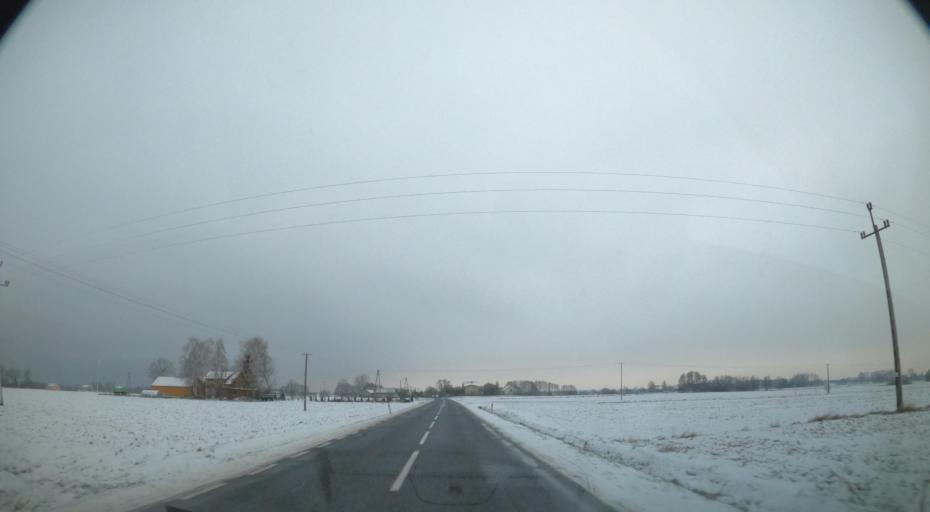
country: PL
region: Masovian Voivodeship
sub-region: Powiat plocki
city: Nowy Duninow
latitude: 52.6281
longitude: 19.4286
